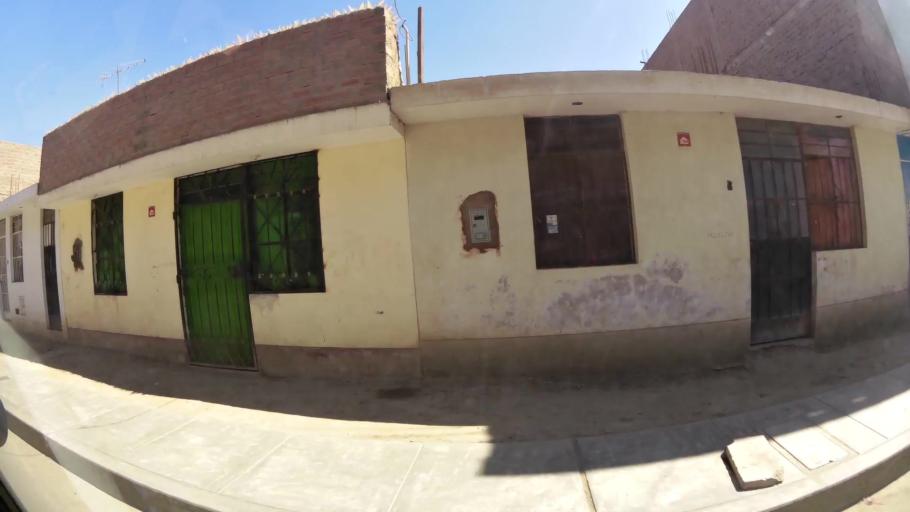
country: PE
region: Ica
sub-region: Provincia de Ica
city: Ica
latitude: -14.0564
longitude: -75.7240
